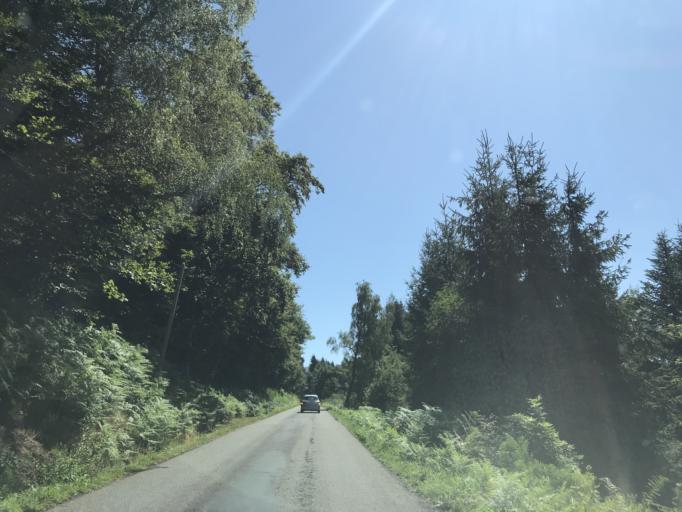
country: FR
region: Auvergne
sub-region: Departement du Puy-de-Dome
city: Job
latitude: 45.6774
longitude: 3.7521
